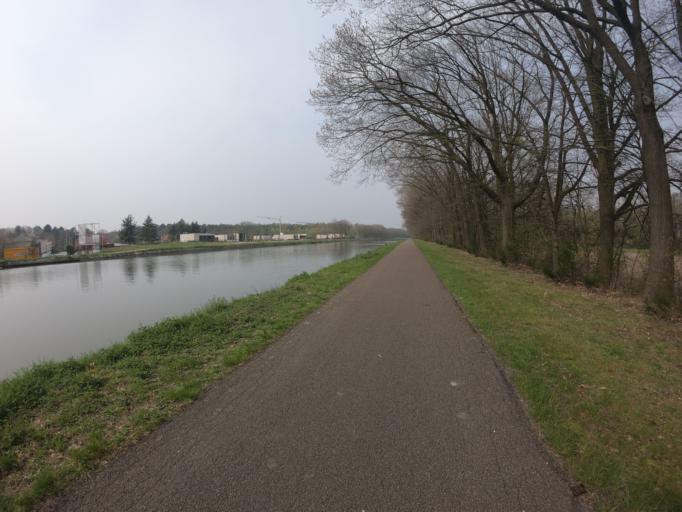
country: BE
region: Flanders
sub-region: Provincie Limburg
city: Maasmechelen
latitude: 51.0232
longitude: 5.7121
